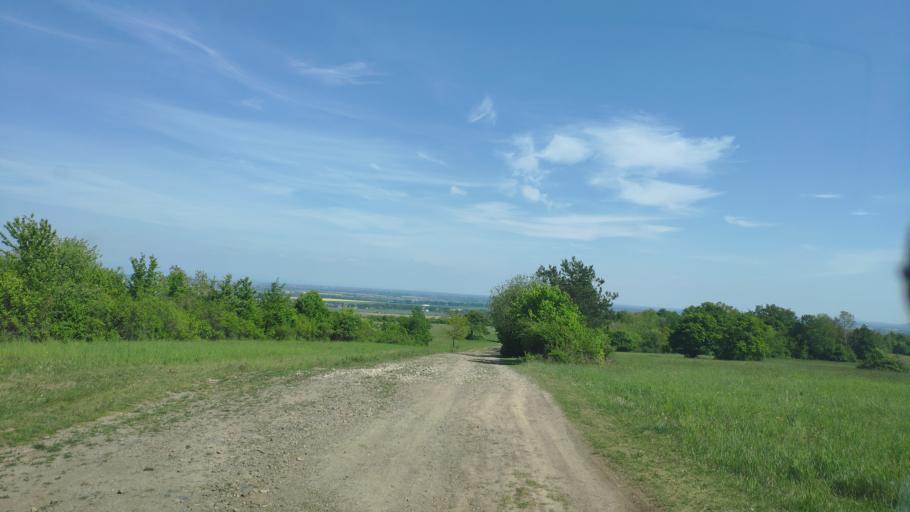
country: SK
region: Kosicky
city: Secovce
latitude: 48.7002
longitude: 21.5900
